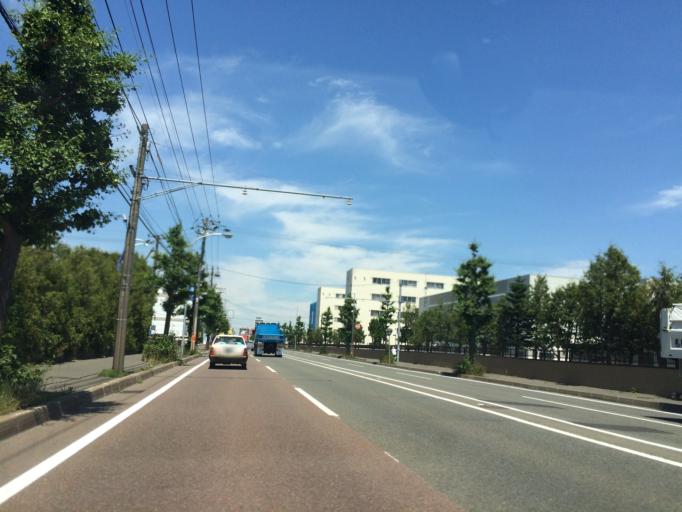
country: JP
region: Hokkaido
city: Sapporo
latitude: 43.0247
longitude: 141.3456
